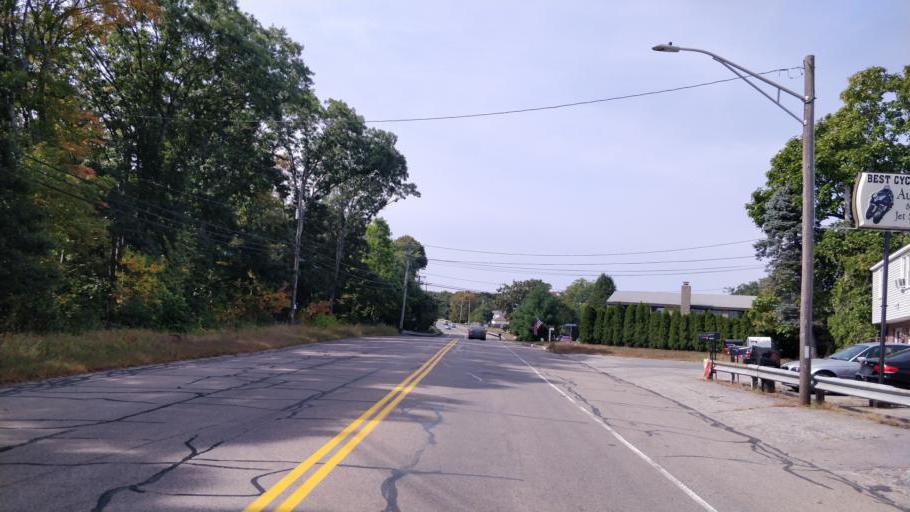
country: US
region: Massachusetts
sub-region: Bristol County
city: North Seekonk
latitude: 41.9022
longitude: -71.3414
